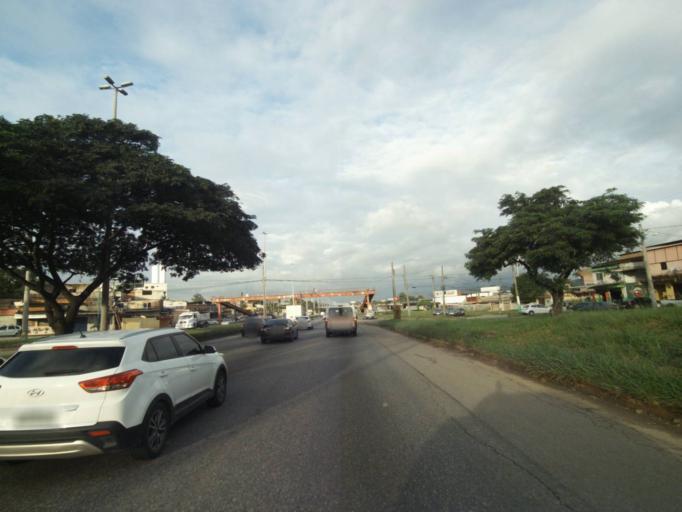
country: BR
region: Rio de Janeiro
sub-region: Nilopolis
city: Nilopolis
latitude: -22.8628
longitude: -43.4421
